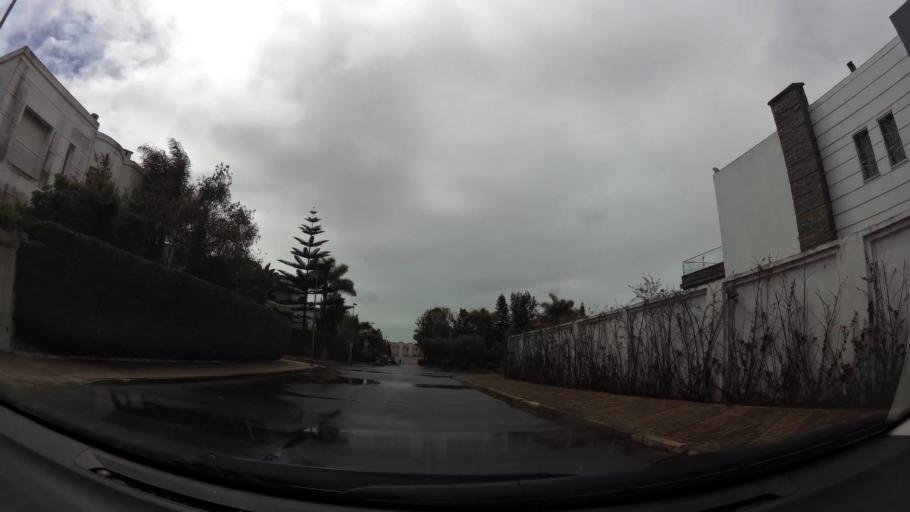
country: MA
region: Grand Casablanca
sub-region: Casablanca
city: Casablanca
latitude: 33.5329
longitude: -7.6403
